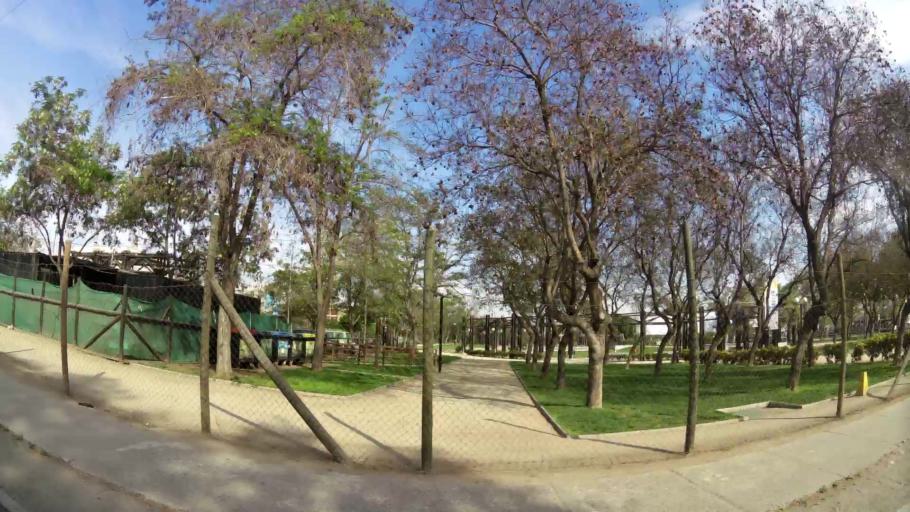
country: CL
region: Santiago Metropolitan
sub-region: Provincia de Santiago
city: La Pintana
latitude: -33.5431
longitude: -70.6368
